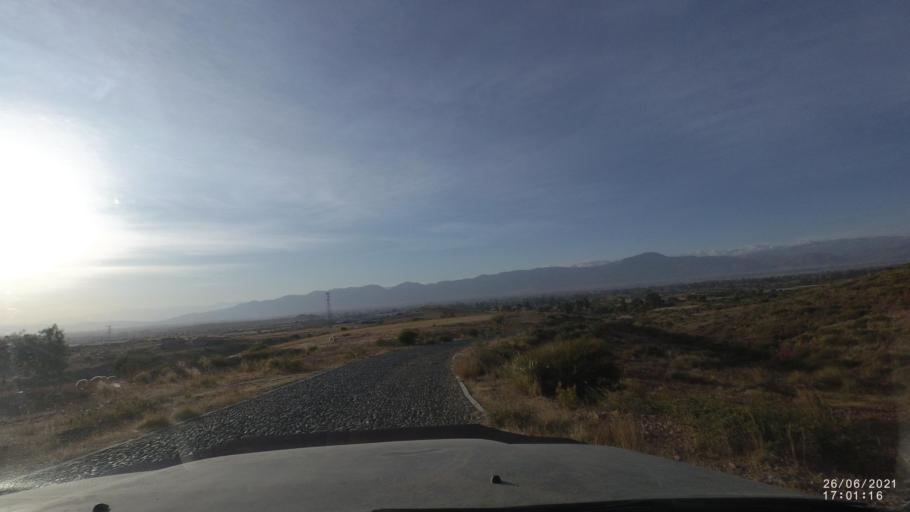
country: BO
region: Cochabamba
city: Cliza
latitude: -17.6631
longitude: -65.9111
